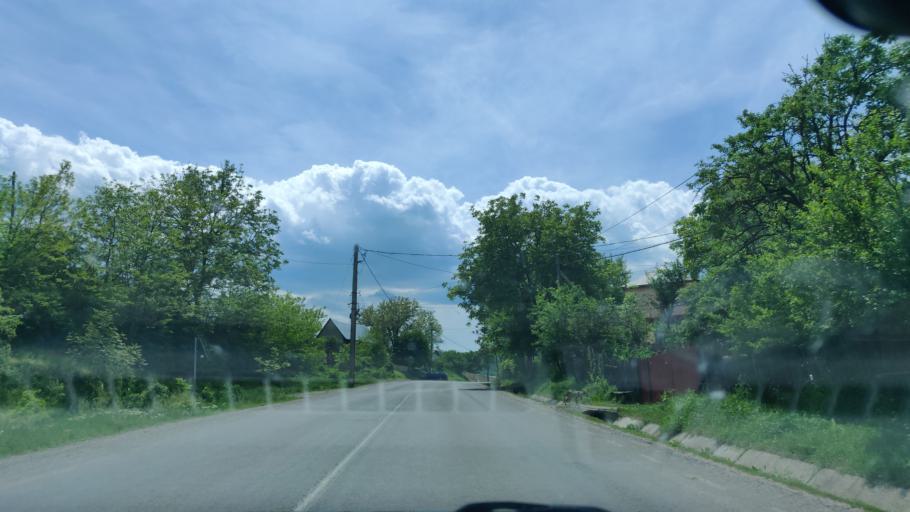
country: RO
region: Vrancea
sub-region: Comuna Vidra
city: Vidra
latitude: 45.9040
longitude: 26.8924
